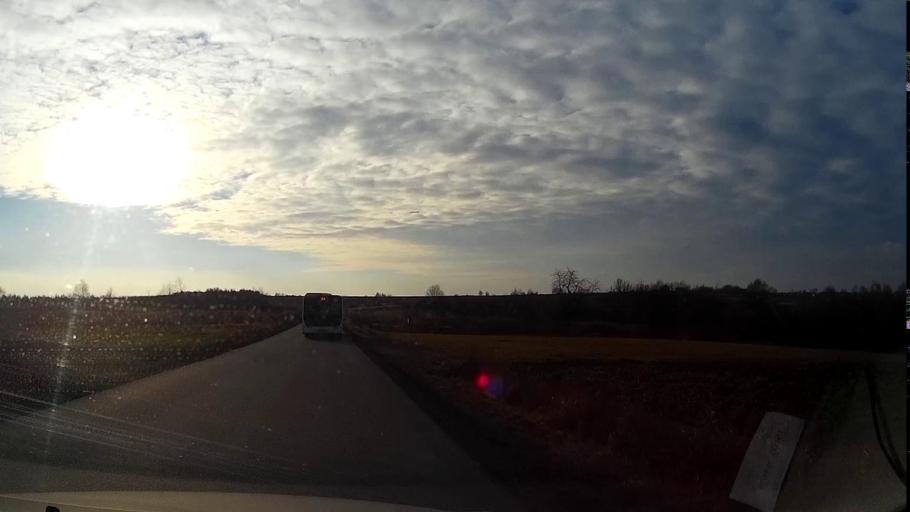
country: PL
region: Lesser Poland Voivodeship
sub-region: Powiat krakowski
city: Sanka
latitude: 50.0625
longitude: 19.6700
